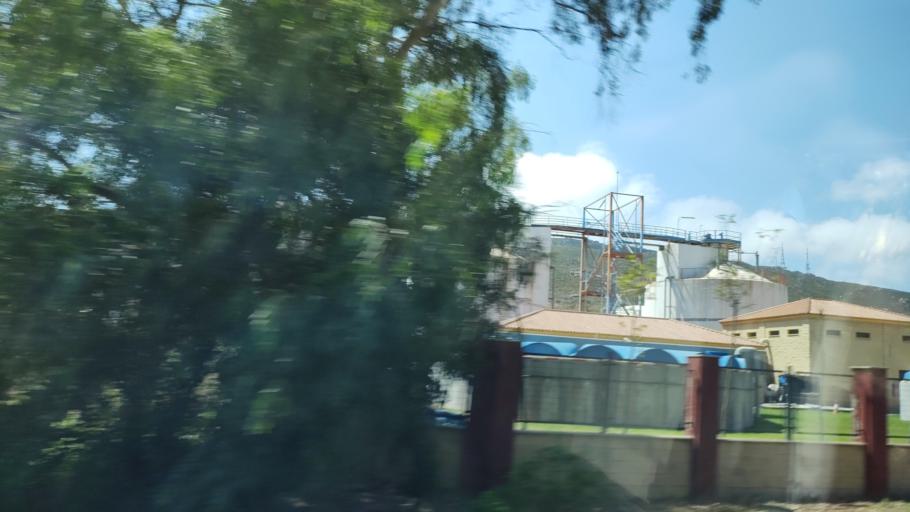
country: ES
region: Andalusia
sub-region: Provincia de Cadiz
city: La Linea de la Concepcion
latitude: 36.1932
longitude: -5.3485
